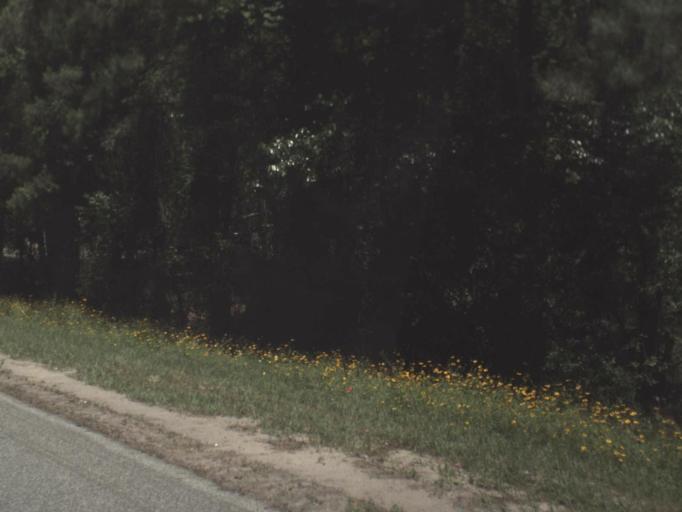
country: US
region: Florida
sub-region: Suwannee County
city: Live Oak
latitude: 30.3788
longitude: -83.1687
